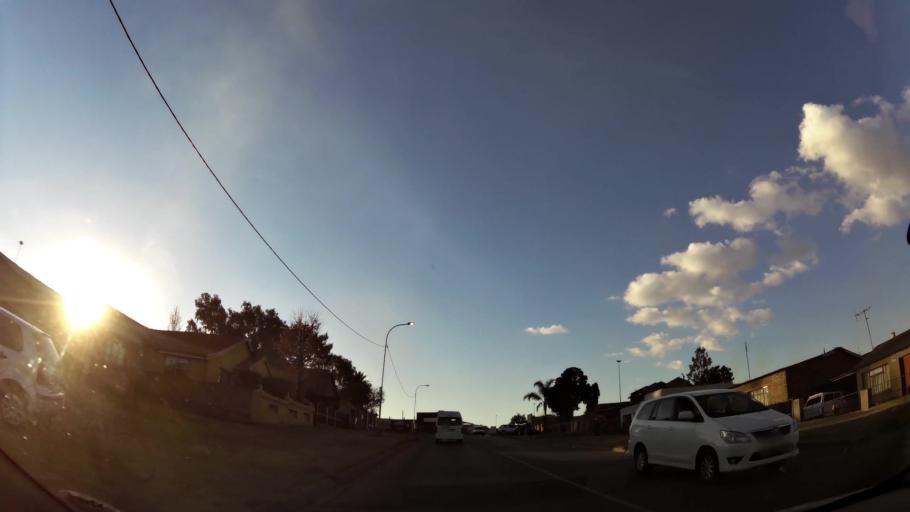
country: ZA
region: Mpumalanga
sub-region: Nkangala District Municipality
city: Witbank
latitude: -25.8744
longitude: 29.1821
